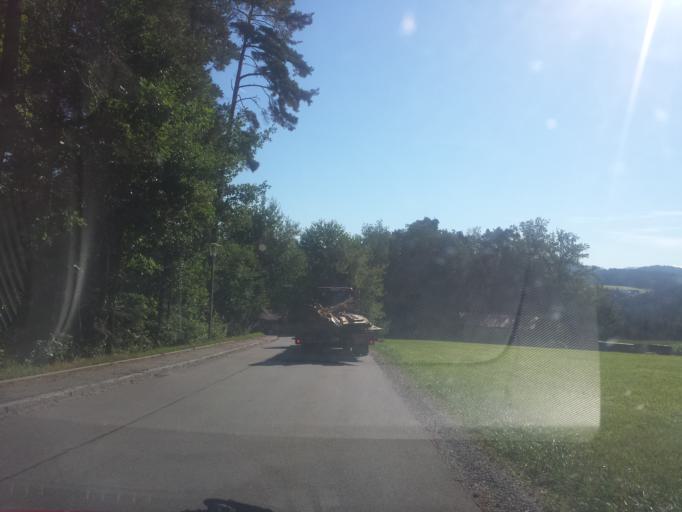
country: DE
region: Bavaria
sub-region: Lower Bavaria
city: Viechtach
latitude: 49.0644
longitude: 12.9023
